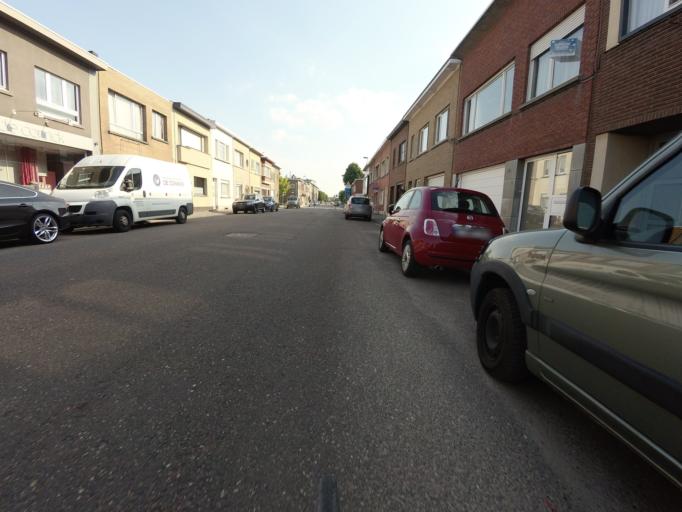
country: BE
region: Flanders
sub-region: Provincie Antwerpen
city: Mortsel
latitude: 51.1966
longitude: 4.4523
